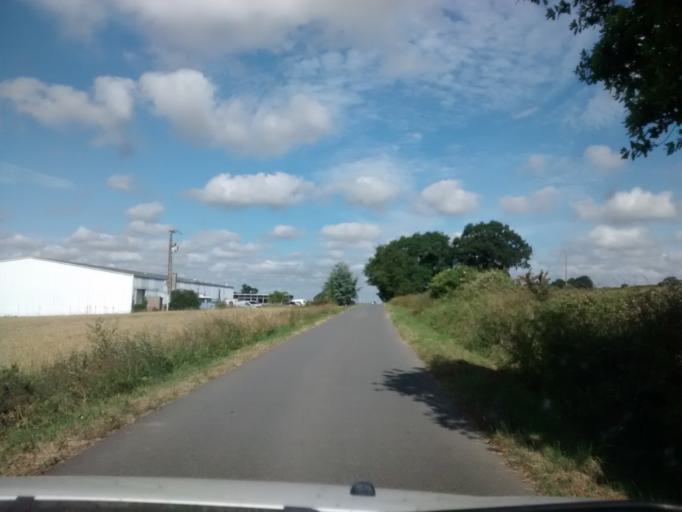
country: FR
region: Brittany
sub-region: Departement d'Ille-et-Vilaine
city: Bain-de-Bretagne
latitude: 47.8248
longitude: -1.6973
